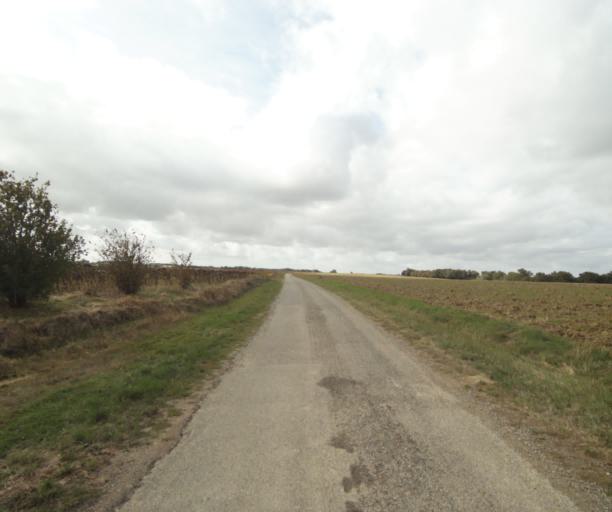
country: FR
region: Midi-Pyrenees
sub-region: Departement du Tarn-et-Garonne
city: Beaumont-de-Lomagne
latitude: 43.8764
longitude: 1.0750
